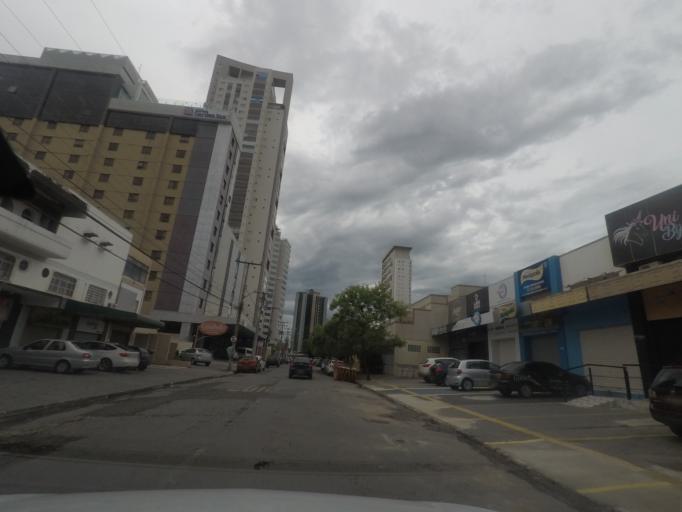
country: BR
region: Goias
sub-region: Goiania
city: Goiania
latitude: -16.6903
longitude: -49.2662
